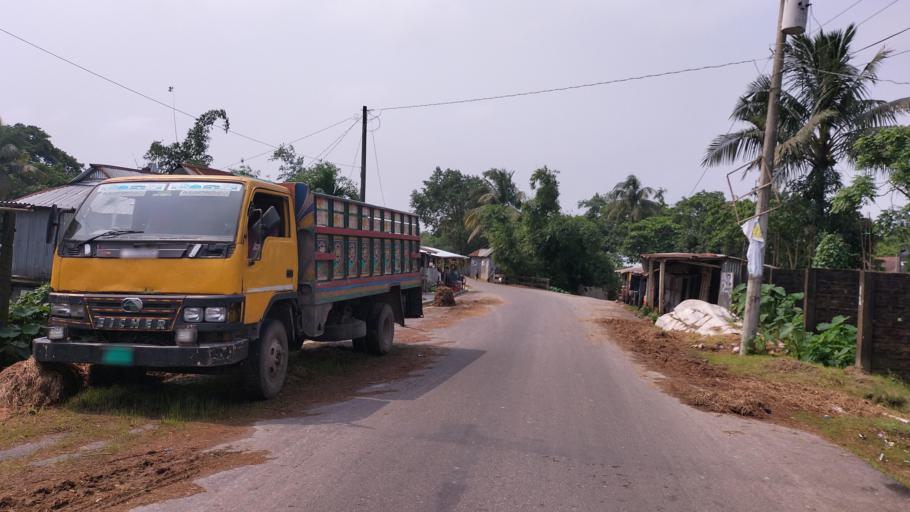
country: BD
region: Dhaka
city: Netrakona
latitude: 24.9576
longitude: 90.8350
